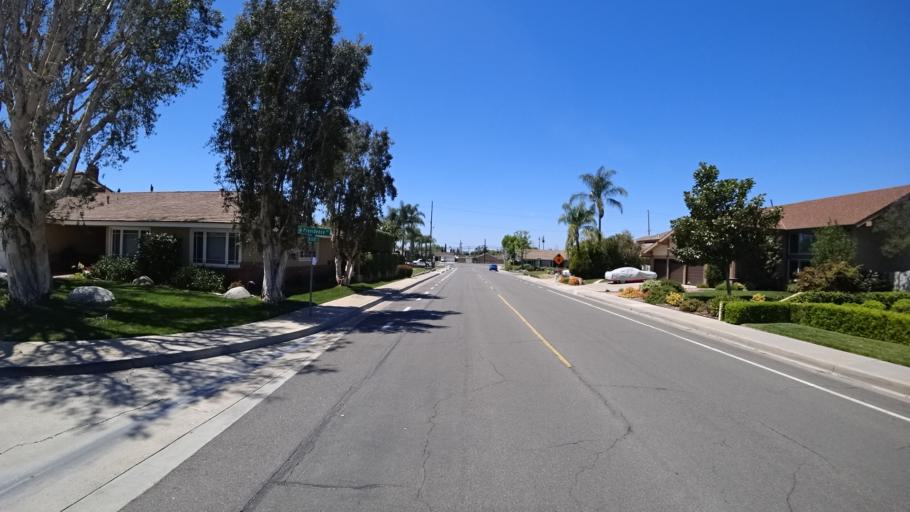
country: US
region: California
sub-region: Orange County
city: Villa Park
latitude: 33.8078
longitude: -117.8205
